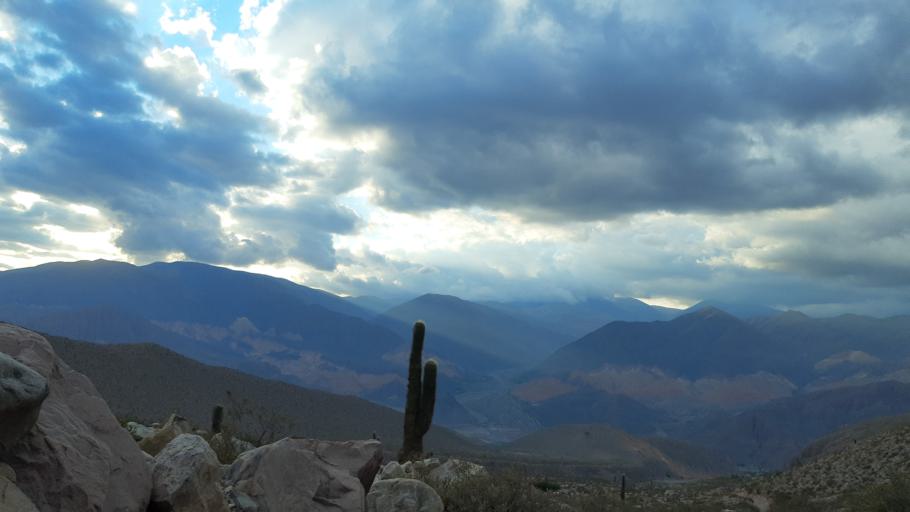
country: AR
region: Jujuy
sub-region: Departamento de Tilcara
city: Tilcara
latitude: -23.5932
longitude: -65.3808
